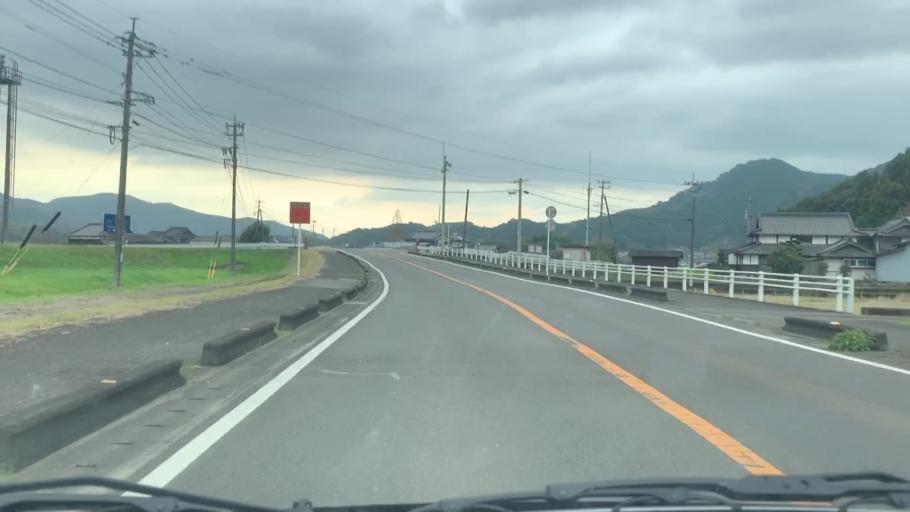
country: JP
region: Saga Prefecture
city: Takeocho-takeo
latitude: 33.1758
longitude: 130.0472
